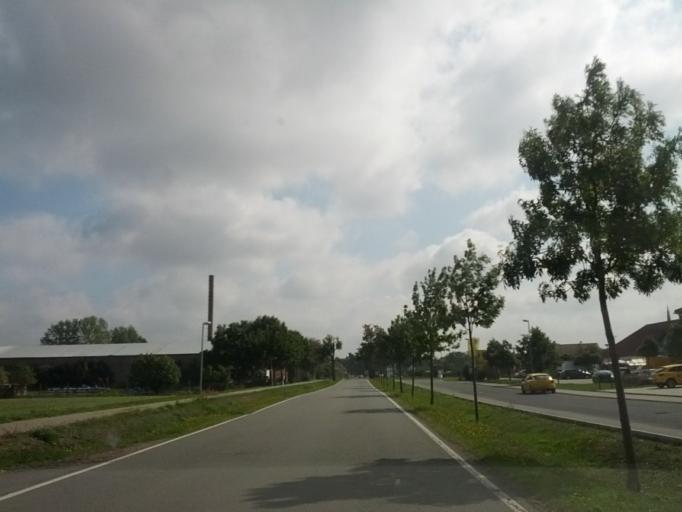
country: DE
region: Thuringia
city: Seebergen
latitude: 50.8976
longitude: 10.7691
